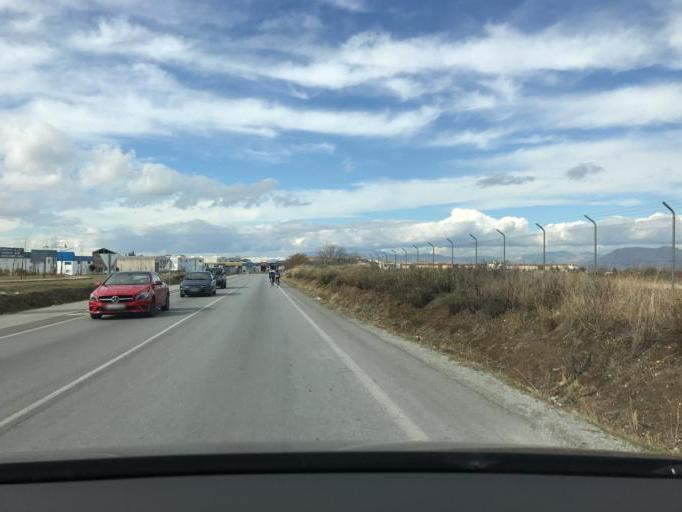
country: ES
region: Andalusia
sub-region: Provincia de Granada
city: Churriana de la Vega
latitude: 37.1347
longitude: -3.6562
